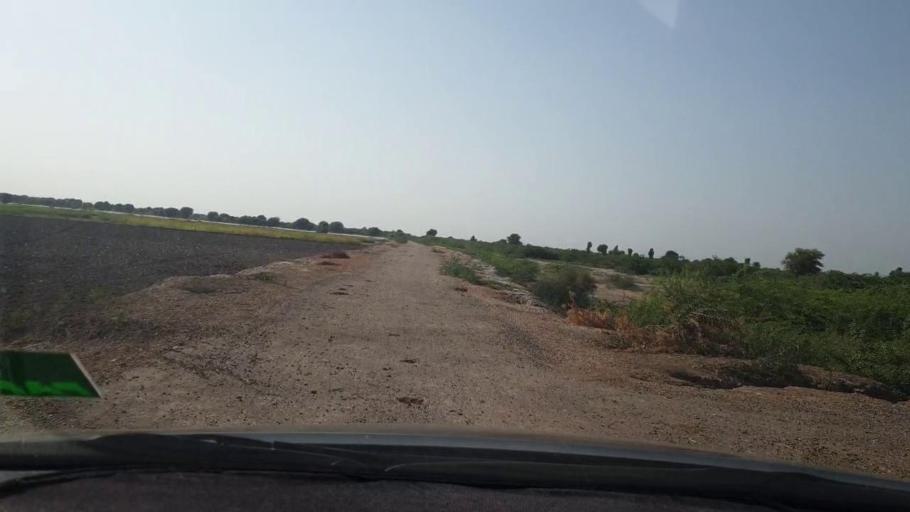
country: PK
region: Sindh
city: Naukot
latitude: 24.8629
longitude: 69.3182
